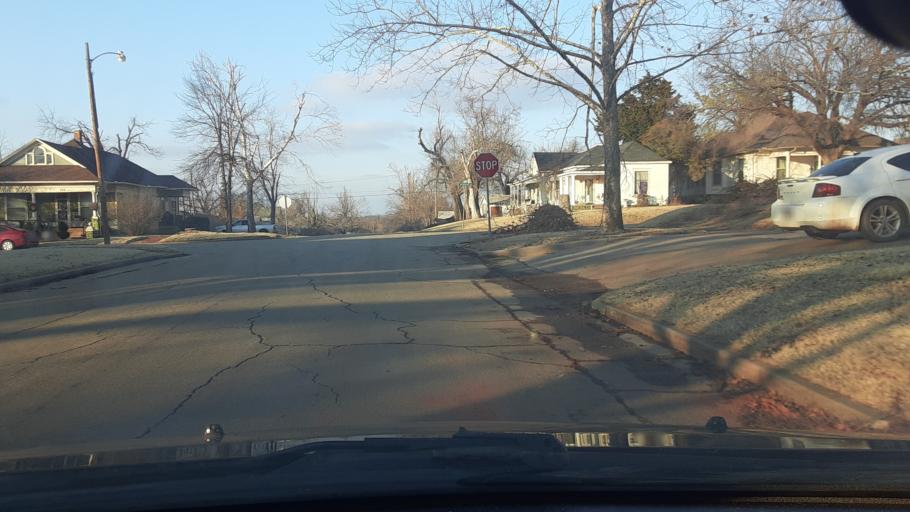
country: US
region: Oklahoma
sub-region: Logan County
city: Guthrie
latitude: 35.8840
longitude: -97.4215
